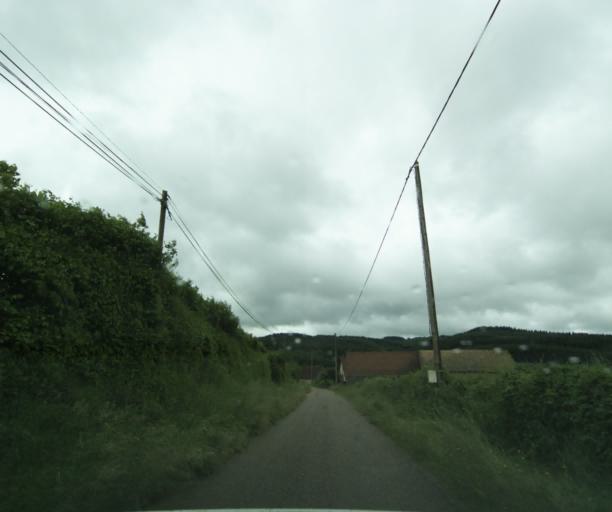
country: FR
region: Bourgogne
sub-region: Departement de Saone-et-Loire
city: Matour
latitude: 46.4553
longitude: 4.4590
